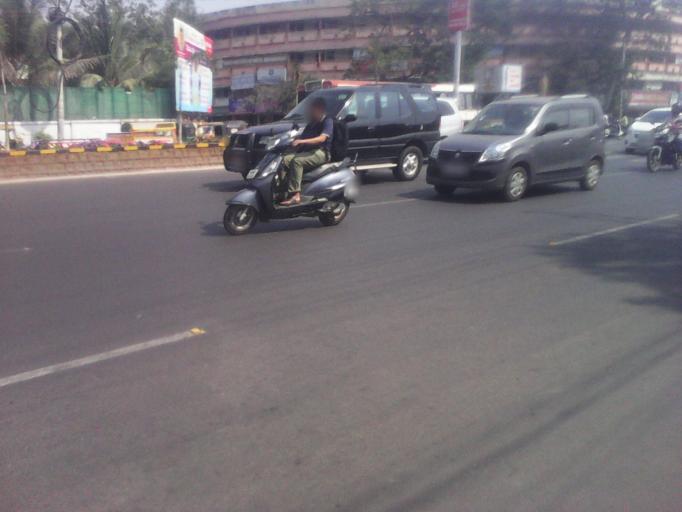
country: IN
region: Andhra Pradesh
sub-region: Krishna
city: Vijayawada
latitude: 16.5042
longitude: 80.6358
